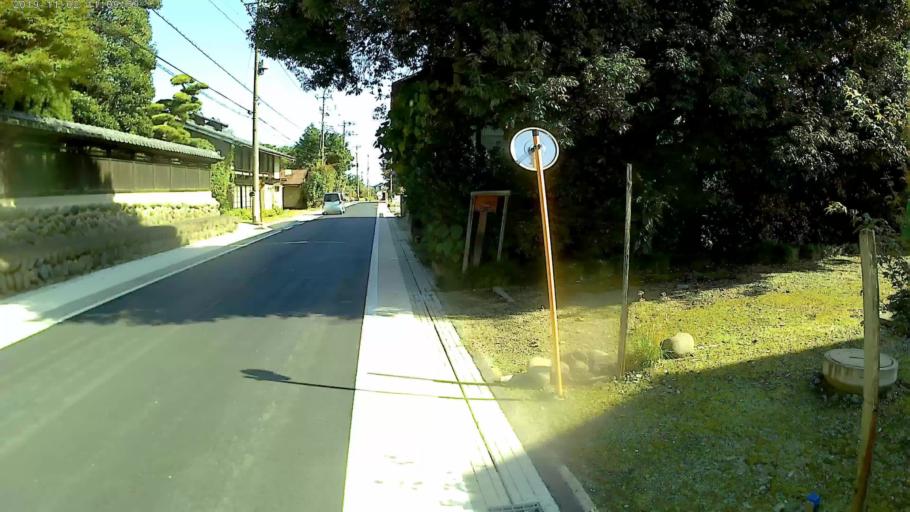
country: JP
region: Gunma
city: Annaka
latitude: 36.3087
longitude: 138.8413
